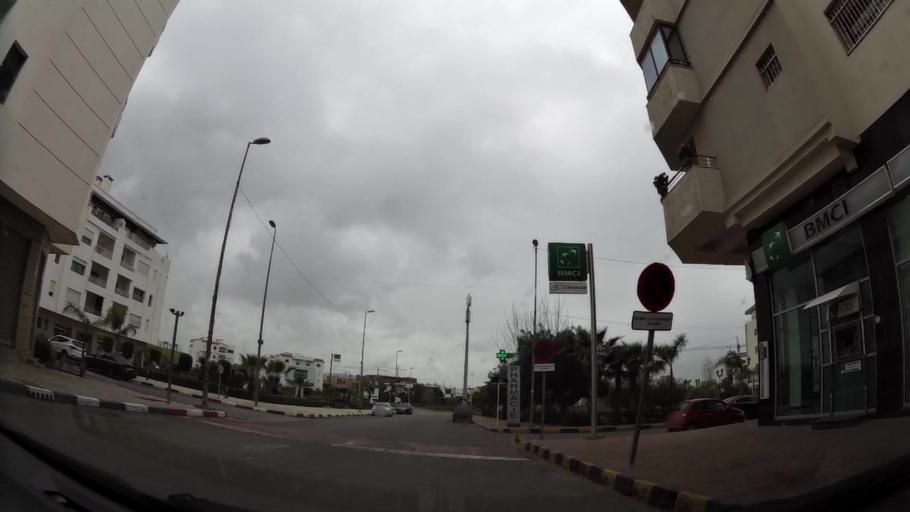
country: MA
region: Grand Casablanca
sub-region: Casablanca
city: Casablanca
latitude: 33.5276
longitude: -7.6130
